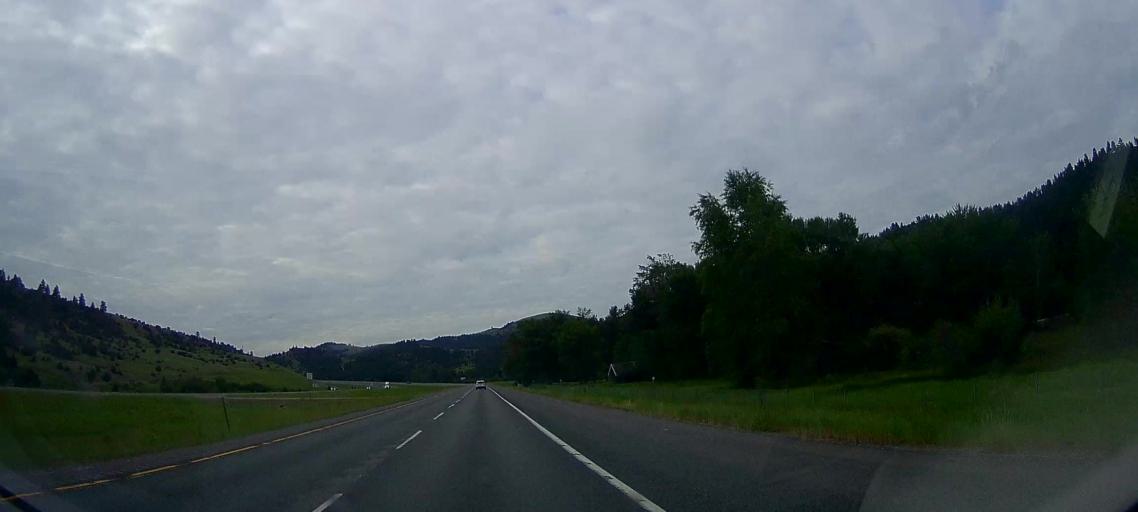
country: US
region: Montana
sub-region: Powell County
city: Deer Lodge
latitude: 46.5632
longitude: -112.8880
